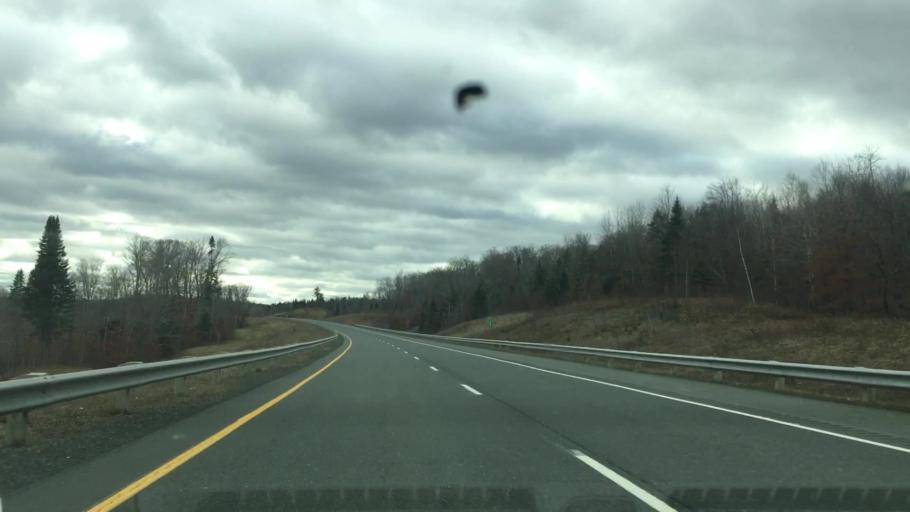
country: US
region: Maine
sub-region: Aroostook County
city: Fort Fairfield
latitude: 46.6473
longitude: -67.7432
